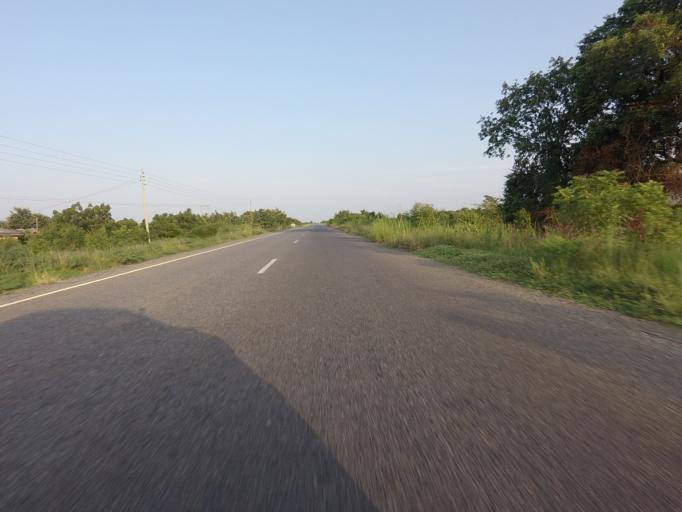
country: GH
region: Volta
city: Anloga
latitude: 5.8879
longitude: 0.7218
